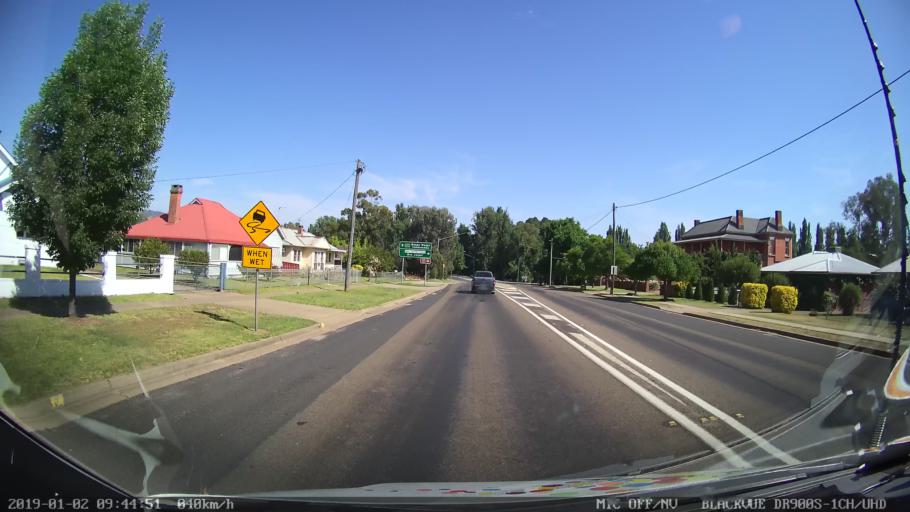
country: AU
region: New South Wales
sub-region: Tumut Shire
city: Tumut
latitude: -35.2977
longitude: 148.2231
